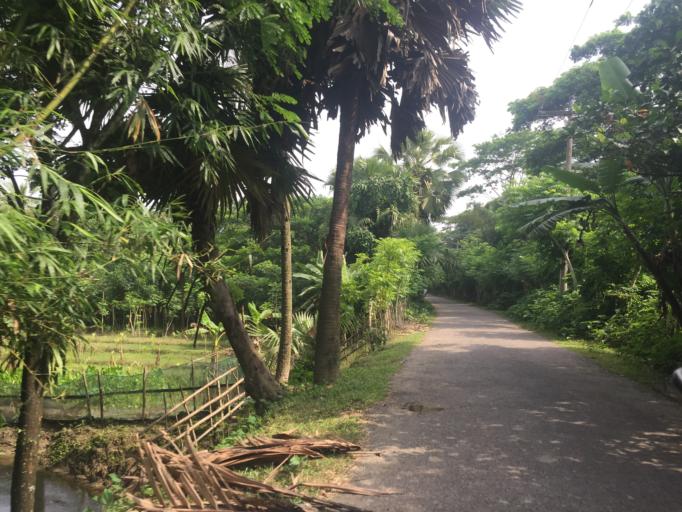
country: BD
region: Barisal
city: Mathba
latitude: 22.2397
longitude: 89.9148
